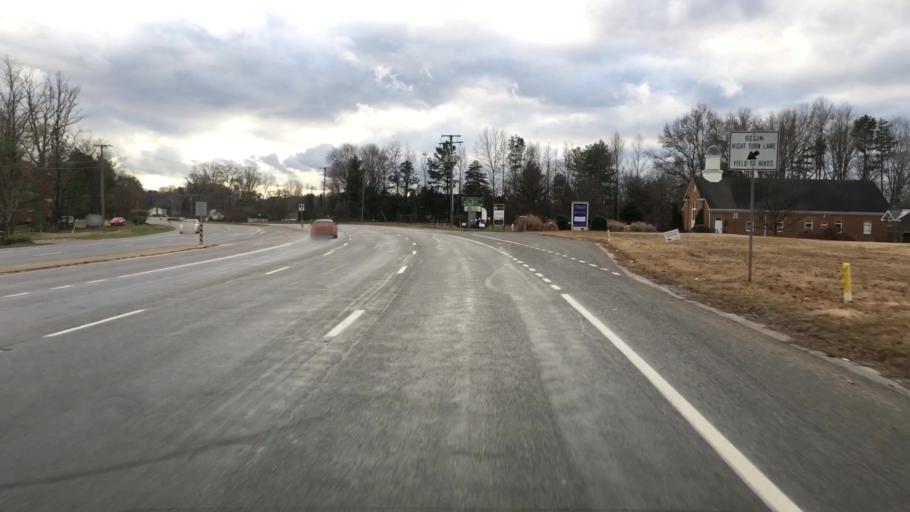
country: US
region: Virginia
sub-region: Chesterfield County
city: Bon Air
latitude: 37.4831
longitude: -77.5982
